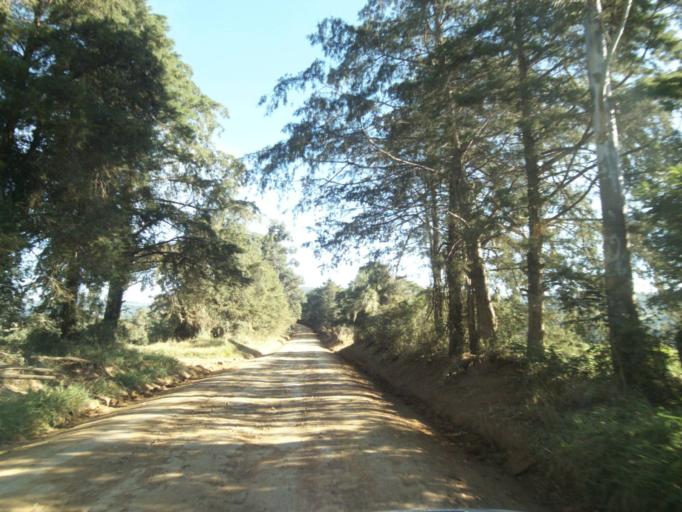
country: BR
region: Parana
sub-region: Tibagi
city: Tibagi
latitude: -24.5295
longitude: -50.5133
